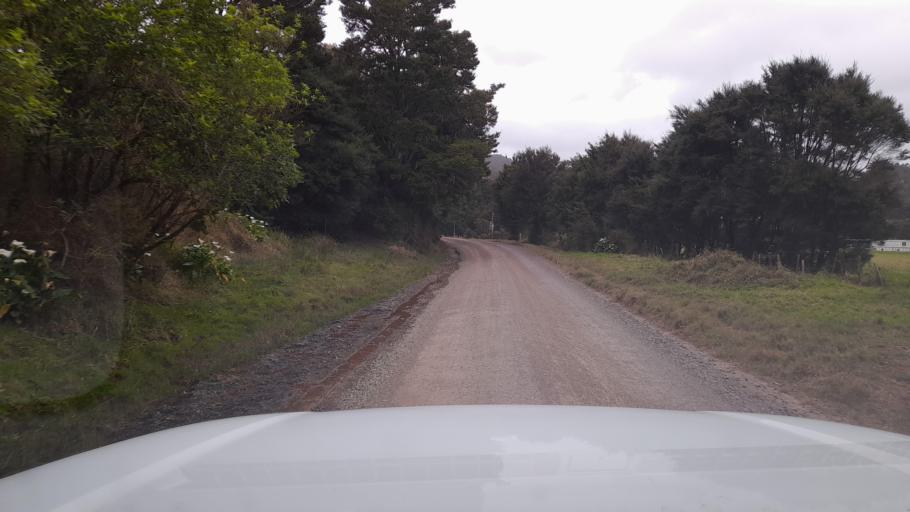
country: NZ
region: Northland
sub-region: Far North District
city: Paihia
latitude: -35.3377
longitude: 174.2331
